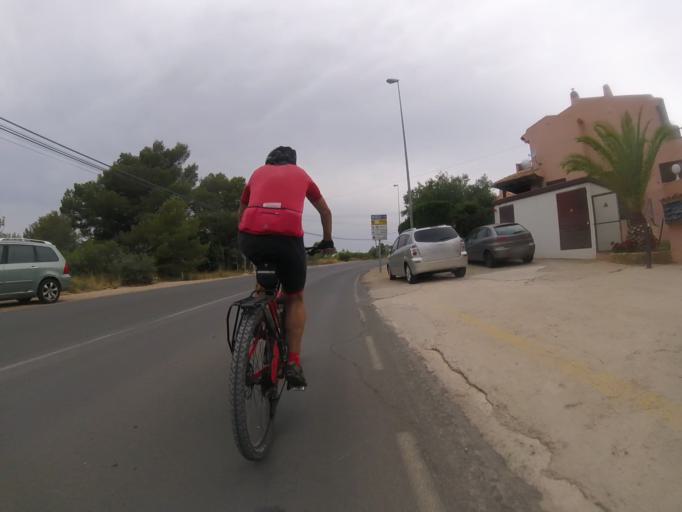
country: ES
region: Valencia
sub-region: Provincia de Castello
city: Alcoceber
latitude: 40.2507
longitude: 0.2768
